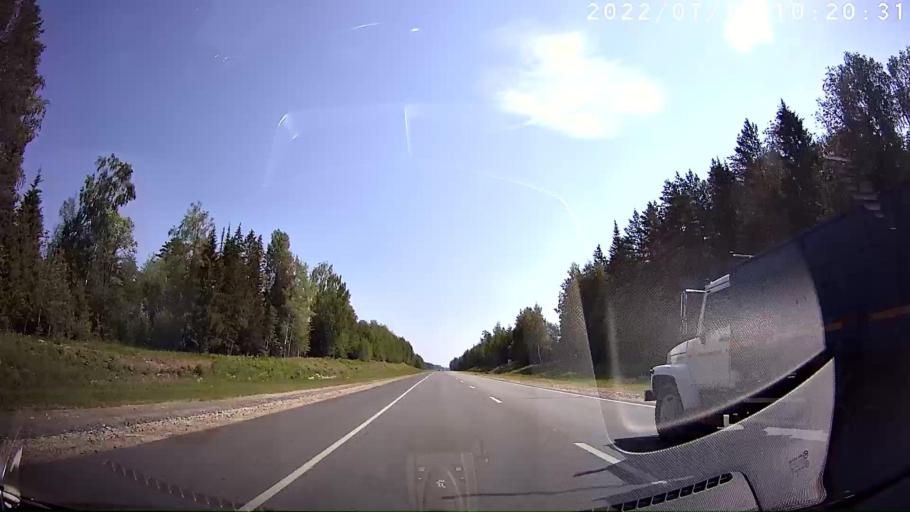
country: RU
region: Mariy-El
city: Sovetskiy
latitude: 56.7436
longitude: 48.4253
